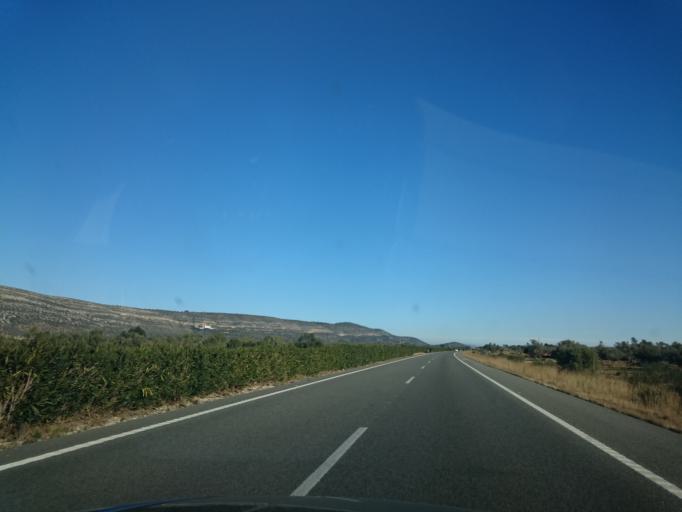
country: ES
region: Catalonia
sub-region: Provincia de Tarragona
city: Ulldecona
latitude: 40.6058
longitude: 0.4745
